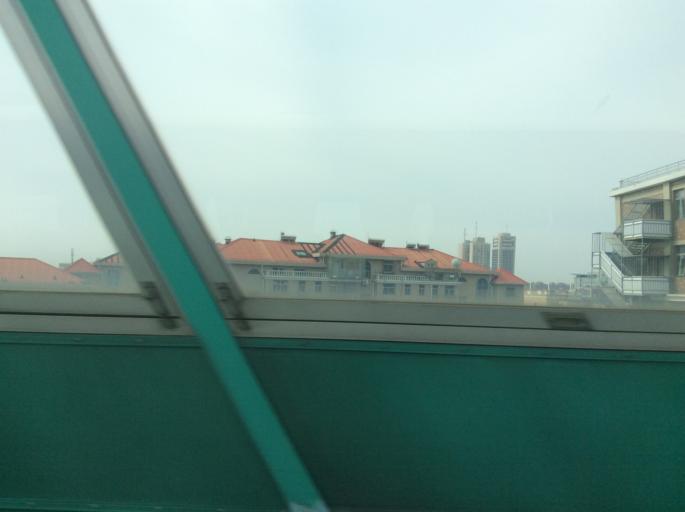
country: CN
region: Shanghai Shi
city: Kangqiao
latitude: 31.2020
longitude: 121.6960
